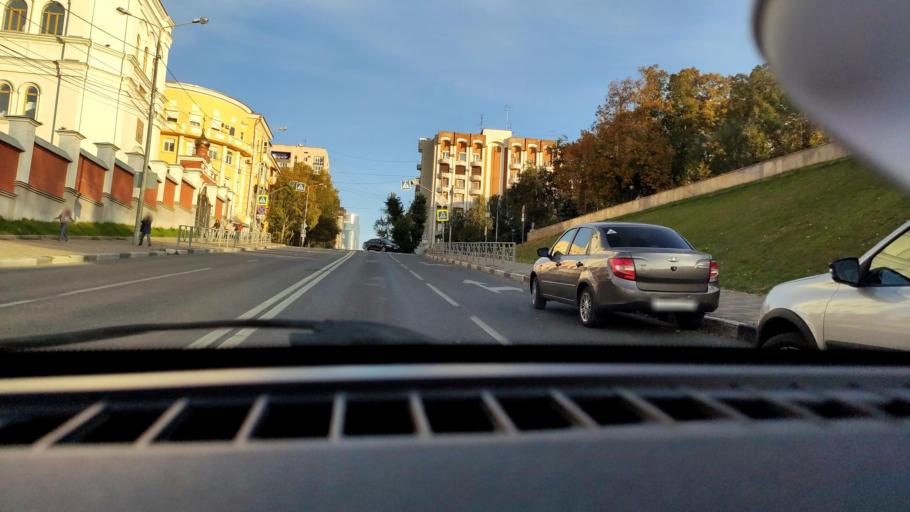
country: RU
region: Samara
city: Samara
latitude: 53.1991
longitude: 50.0976
